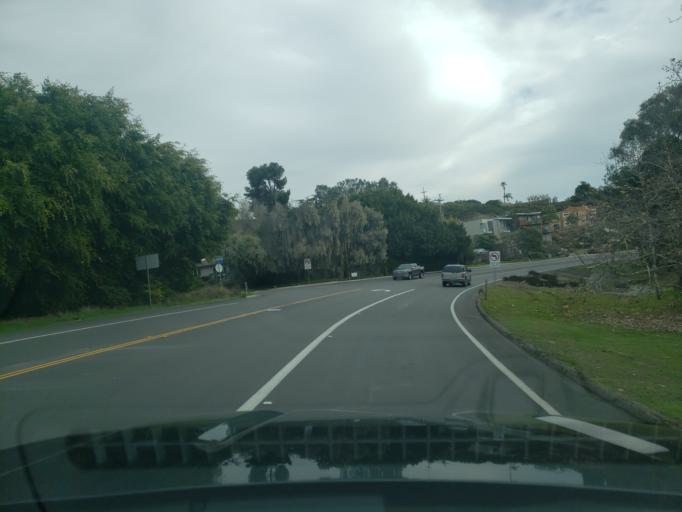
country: US
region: California
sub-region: San Diego County
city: Coronado
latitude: 32.7279
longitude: -117.2403
